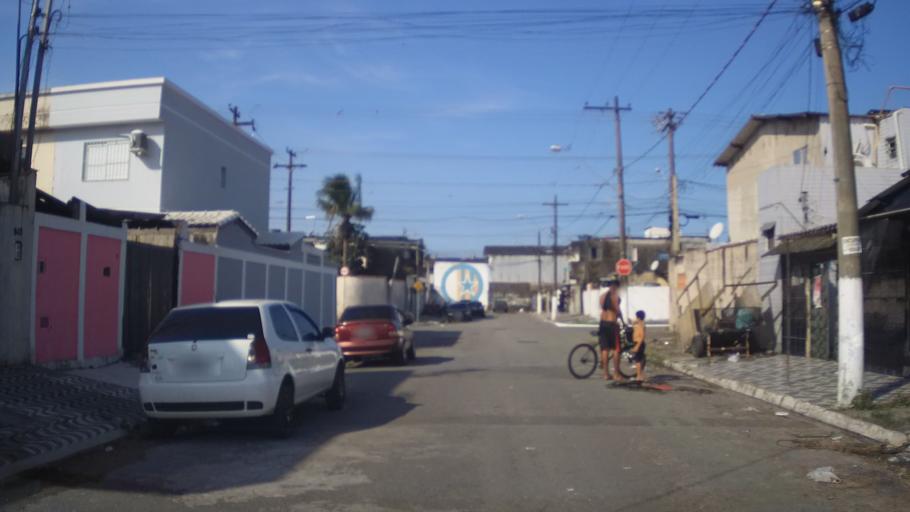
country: BR
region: Sao Paulo
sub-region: Praia Grande
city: Praia Grande
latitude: -24.0072
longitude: -46.4370
